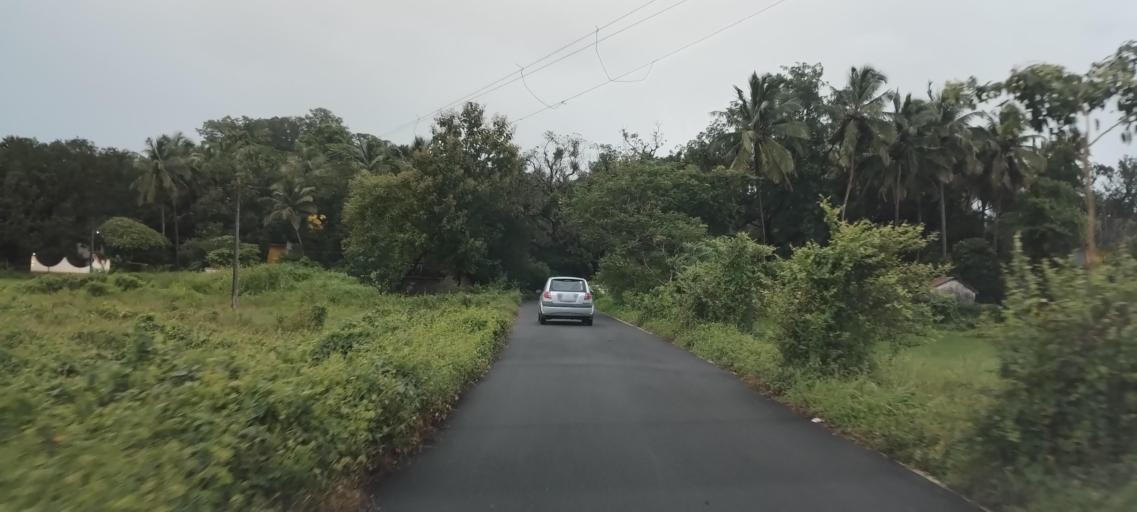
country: IN
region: Goa
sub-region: North Goa
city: Jua
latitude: 15.5195
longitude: 73.8959
